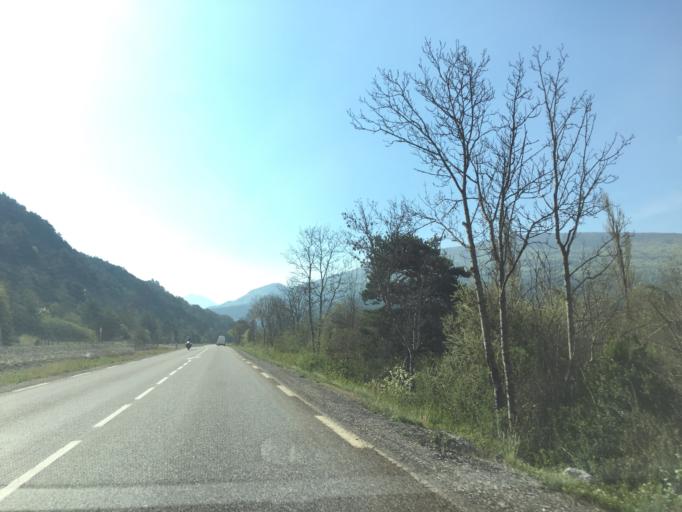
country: FR
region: Provence-Alpes-Cote d'Azur
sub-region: Departement des Hautes-Alpes
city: Veynes
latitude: 44.5742
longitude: 5.7302
